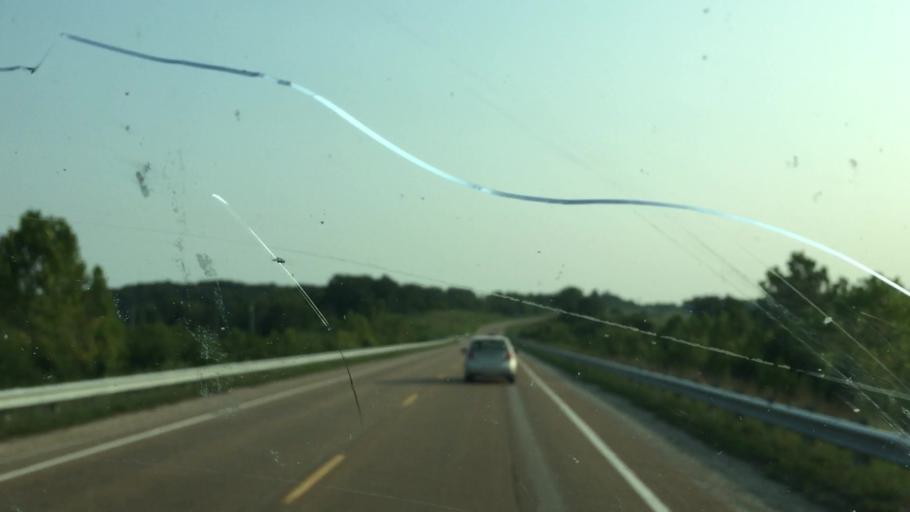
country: US
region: Missouri
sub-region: Pulaski County
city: Richland
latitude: 37.7959
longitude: -92.4064
